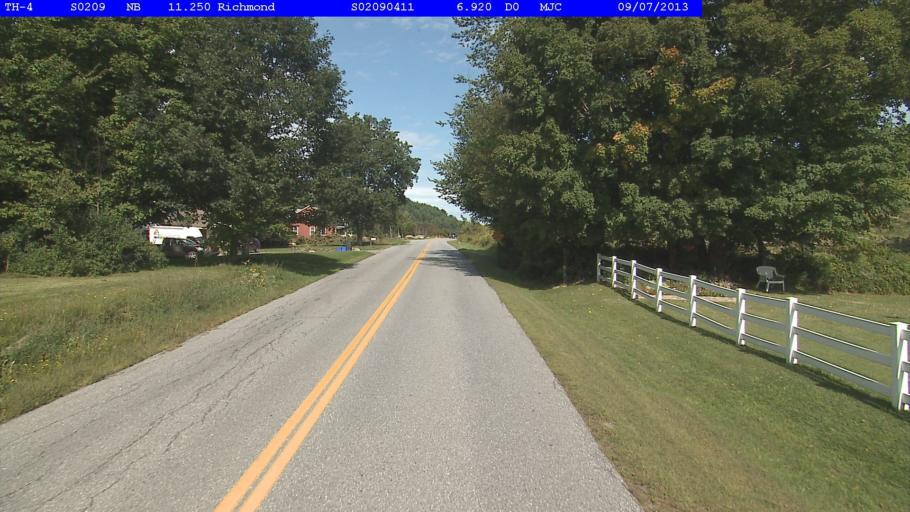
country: US
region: Vermont
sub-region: Chittenden County
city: Jericho
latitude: 44.4240
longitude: -72.9796
